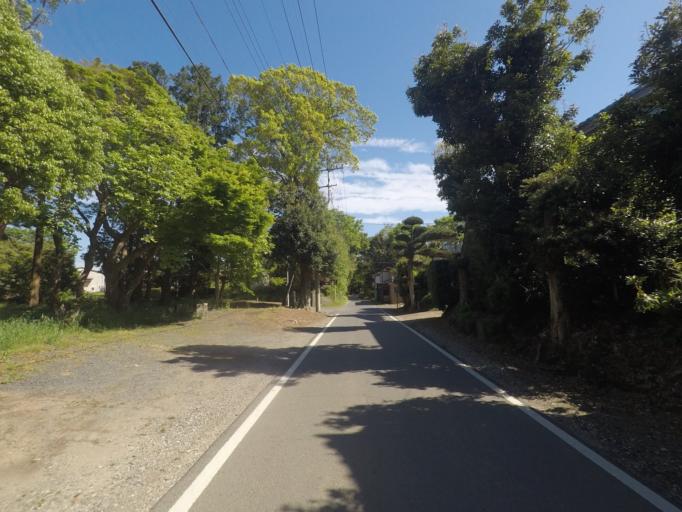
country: JP
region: Ibaraki
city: Itako
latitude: 36.0249
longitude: 140.4713
